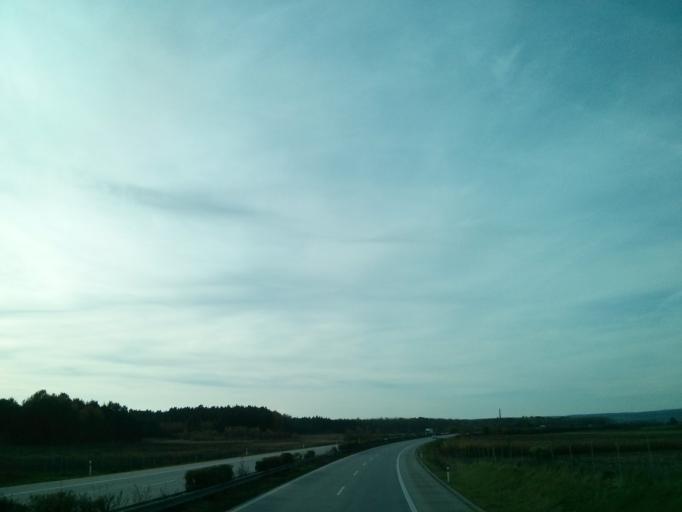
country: CZ
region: Plzensky
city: Nyrany
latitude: 49.7022
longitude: 13.1896
